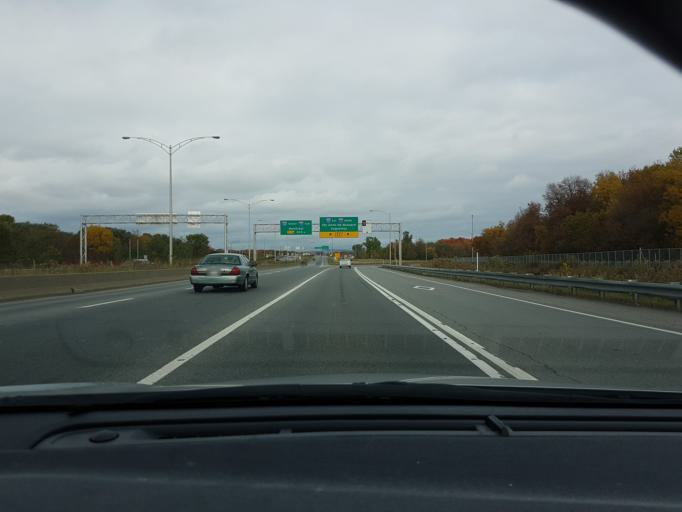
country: CA
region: Quebec
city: L'Ancienne-Lorette
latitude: 46.8199
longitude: -71.2941
